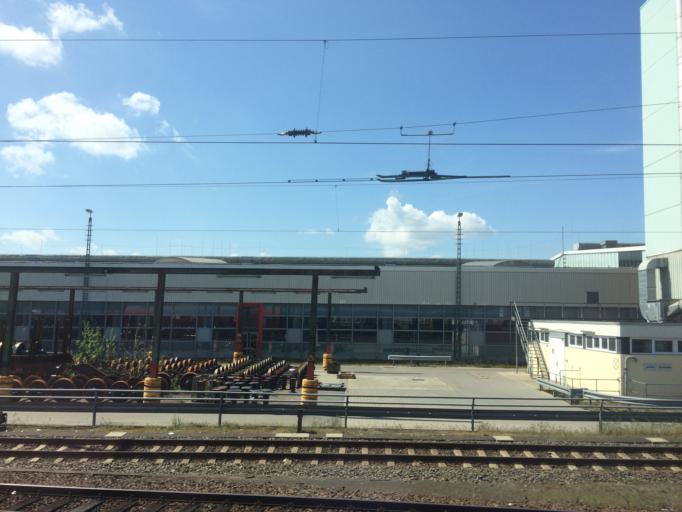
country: DE
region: Hamburg
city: Stellingen
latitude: 53.5851
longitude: 9.9218
